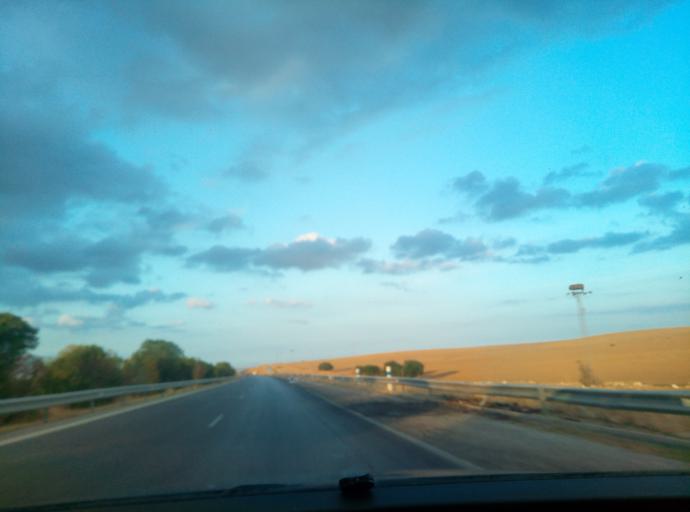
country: TN
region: Tunis
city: Oued Lill
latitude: 36.7060
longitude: 9.9620
